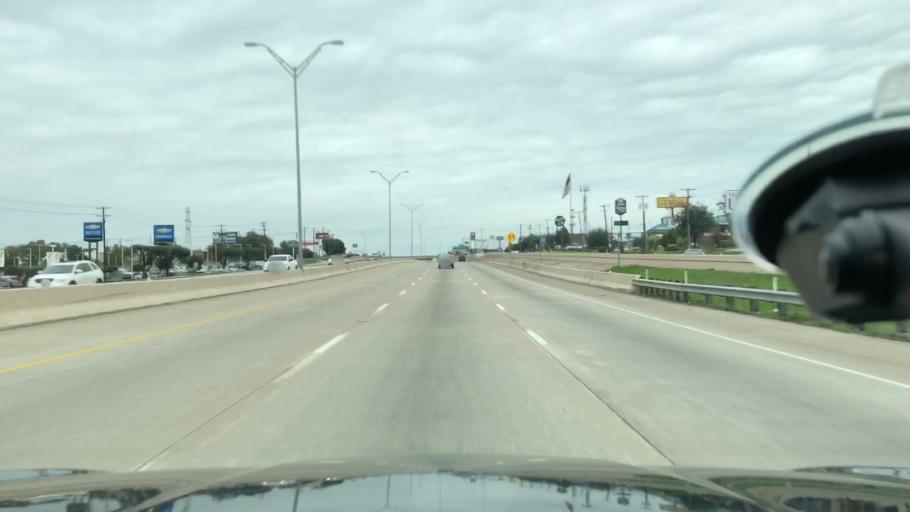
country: US
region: Texas
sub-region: Dallas County
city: DeSoto
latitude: 32.5979
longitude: -96.8224
